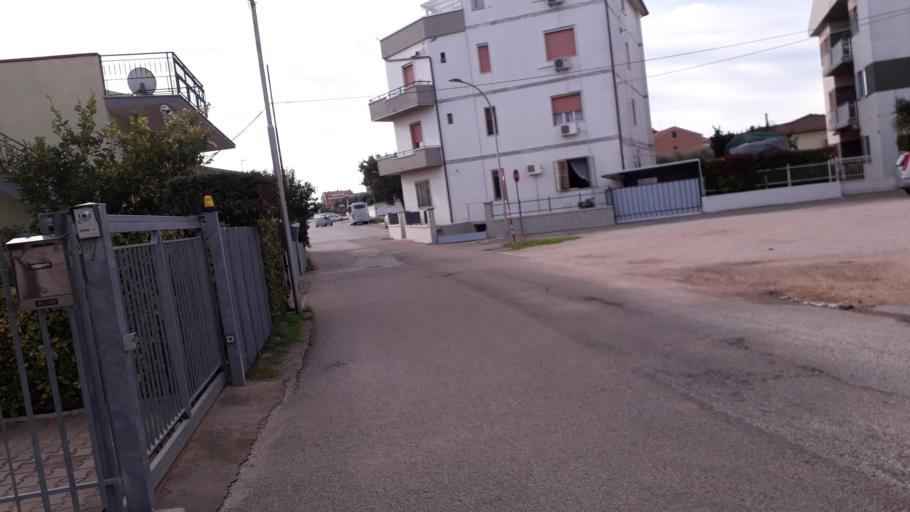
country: IT
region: Molise
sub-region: Provincia di Campobasso
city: Campomarino
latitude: 41.9545
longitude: 15.0319
